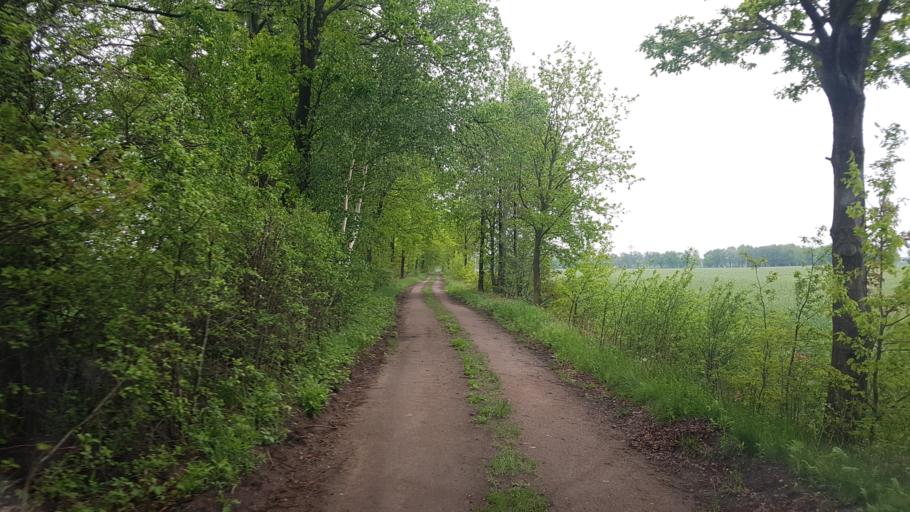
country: DE
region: Brandenburg
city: Elsterwerda
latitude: 51.4390
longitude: 13.5435
